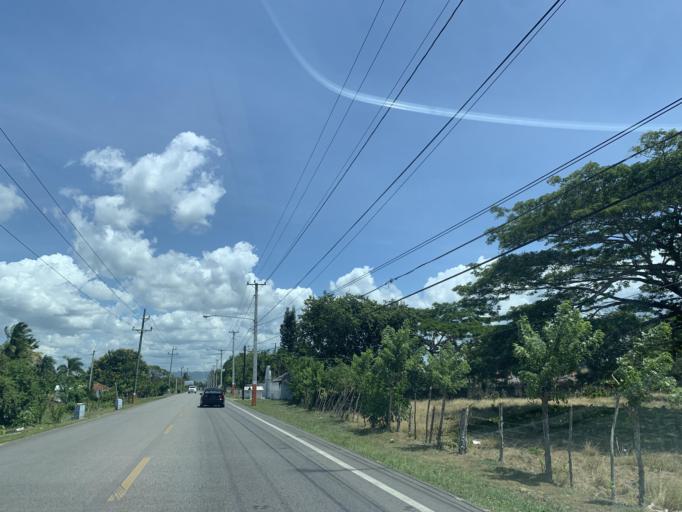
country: DO
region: Puerto Plata
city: Cabarete
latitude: 19.7186
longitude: -70.3863
